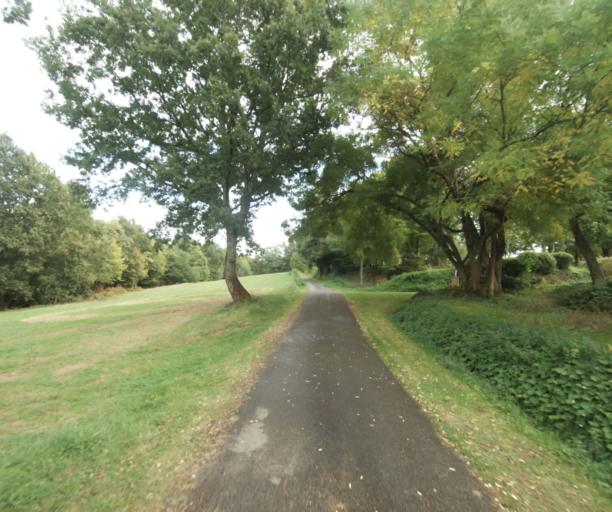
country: FR
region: Midi-Pyrenees
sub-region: Departement du Gers
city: Cazaubon
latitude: 43.8876
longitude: -0.1450
